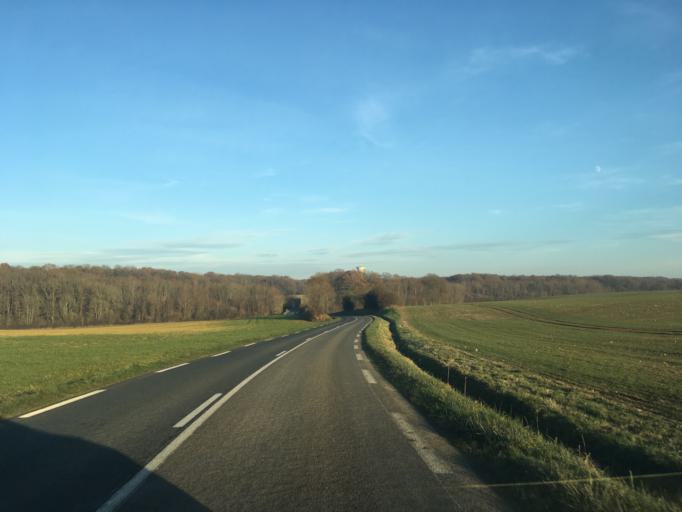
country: FR
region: Haute-Normandie
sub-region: Departement de l'Eure
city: Houlbec-Cocherel
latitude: 49.0626
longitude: 1.3651
